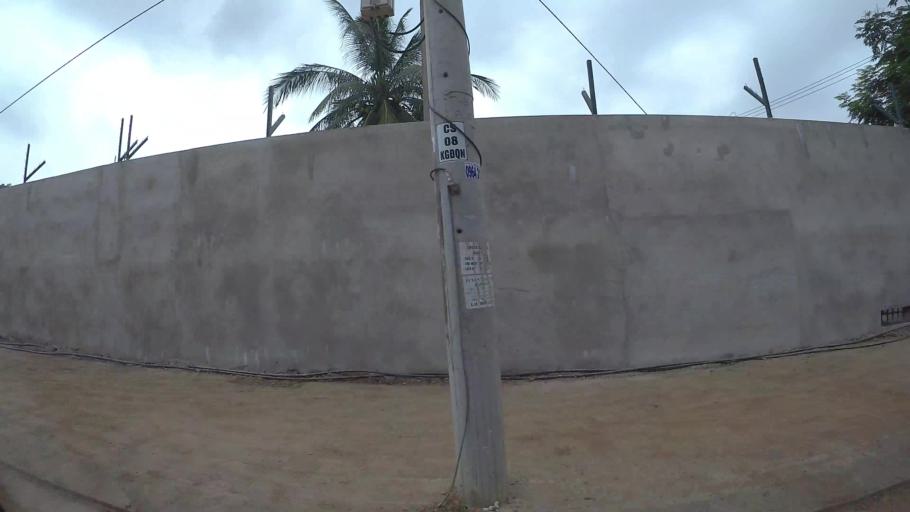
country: VN
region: Da Nang
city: Cam Le
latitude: 16.0343
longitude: 108.1761
